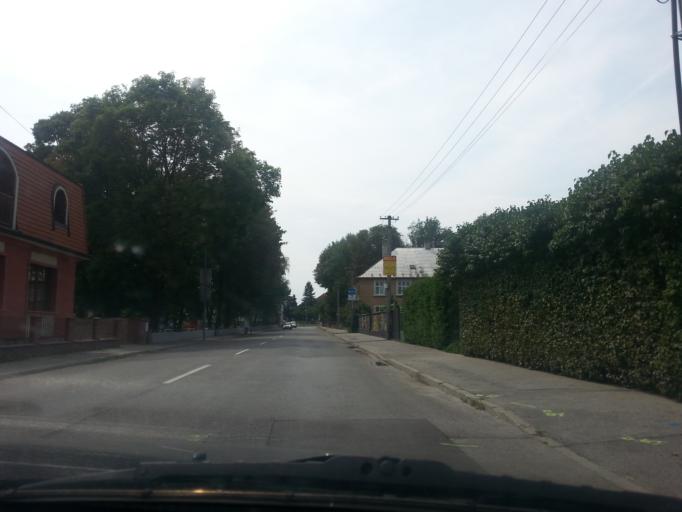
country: SK
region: Trenciansky
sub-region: Okres Nove Mesto nad Vahom
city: Nove Mesto nad Vahom
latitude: 48.7589
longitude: 17.8258
